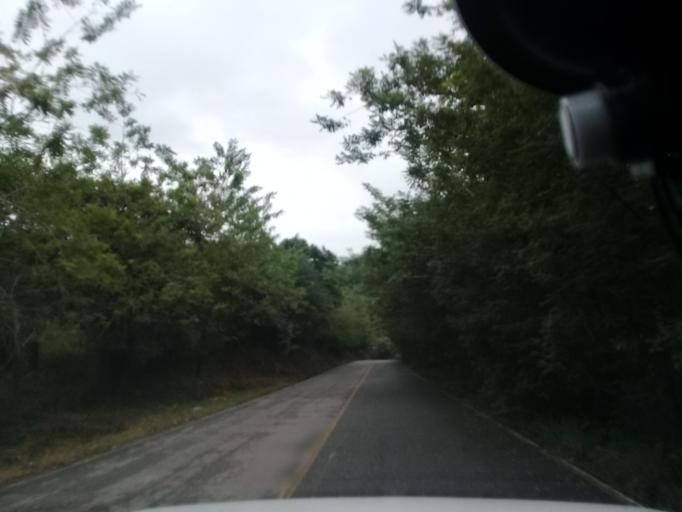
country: MX
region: Veracruz
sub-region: Chalma
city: San Pedro Coyutla
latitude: 21.2107
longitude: -98.4232
